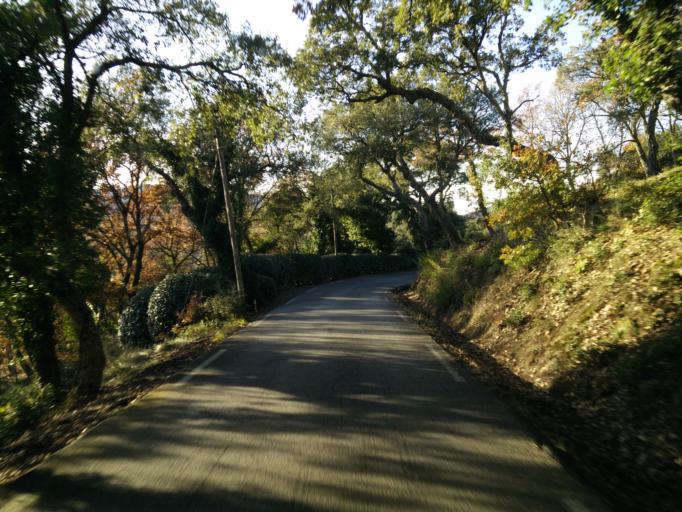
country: FR
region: Provence-Alpes-Cote d'Azur
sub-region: Departement du Var
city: La Garde-Freinet
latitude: 43.3386
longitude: 6.4787
